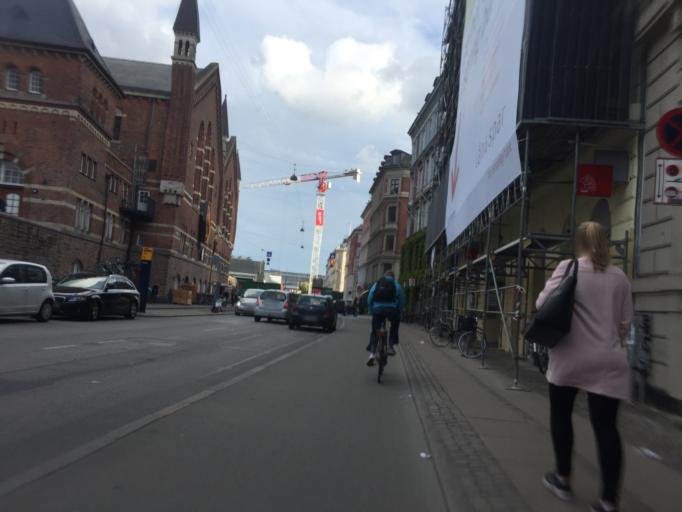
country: DK
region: Capital Region
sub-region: Kobenhavn
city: Copenhagen
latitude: 55.6729
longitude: 12.5632
